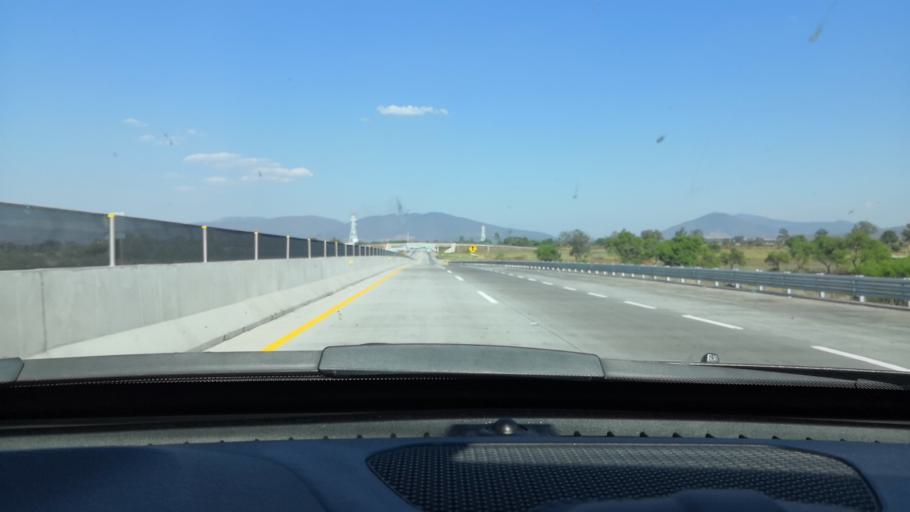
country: MX
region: Jalisco
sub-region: Ixtlahuacan de los Membrillos
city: Los Cedros
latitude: 20.4076
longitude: -103.2296
